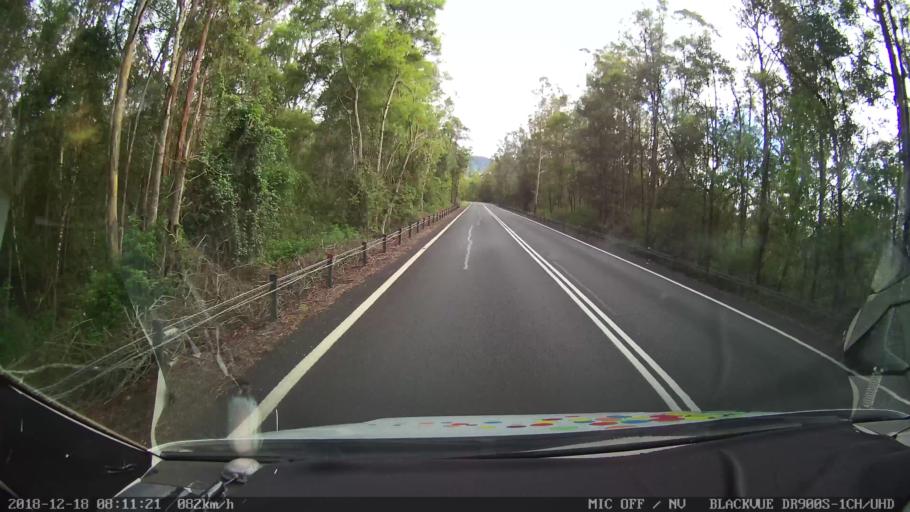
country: AU
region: New South Wales
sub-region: Kyogle
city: Kyogle
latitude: -28.3519
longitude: 152.6685
